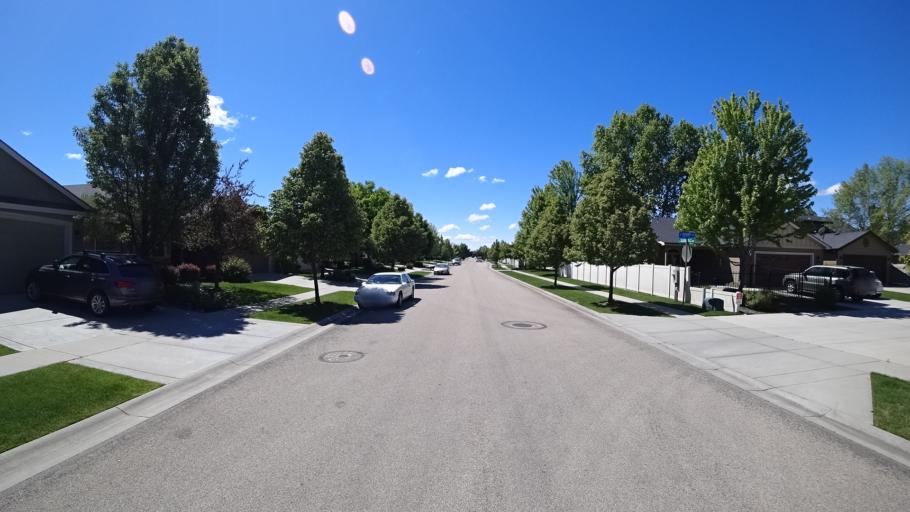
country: US
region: Idaho
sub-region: Ada County
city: Eagle
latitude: 43.6610
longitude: -116.3824
